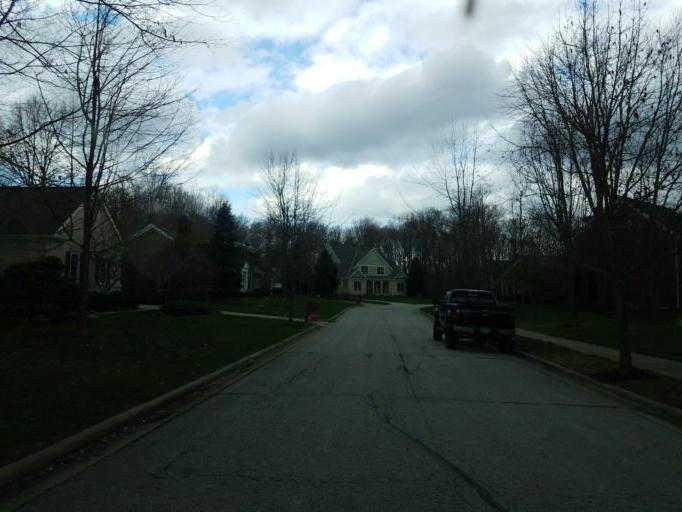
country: US
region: Ohio
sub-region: Delaware County
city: Powell
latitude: 40.1604
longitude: -83.0605
